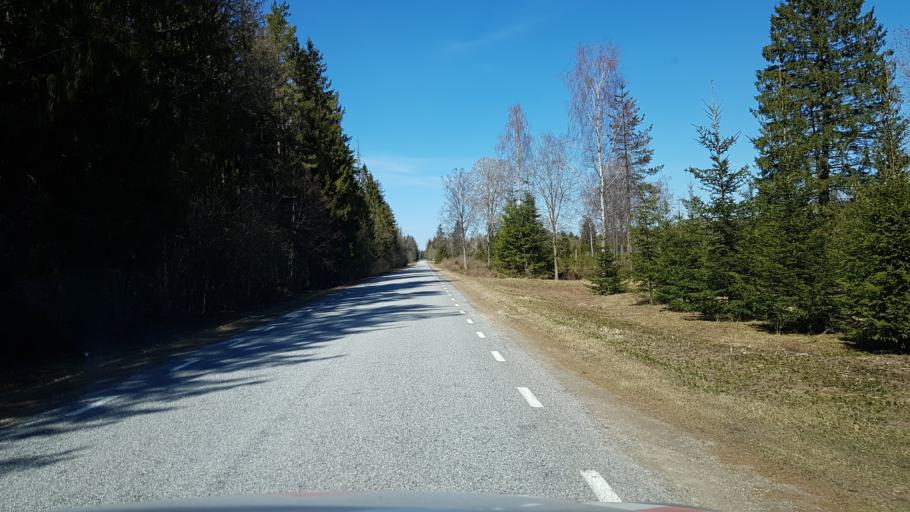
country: EE
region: Laeaene-Virumaa
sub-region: Vinni vald
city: Vinni
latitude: 59.1617
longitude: 26.5123
